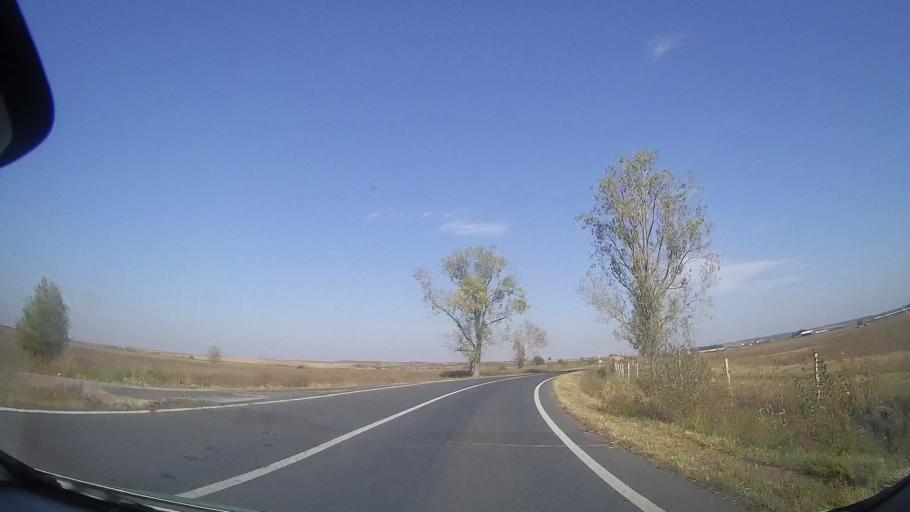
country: RO
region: Timis
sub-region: Comuna Ghizela
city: Ghizela
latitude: 45.7843
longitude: 21.7315
